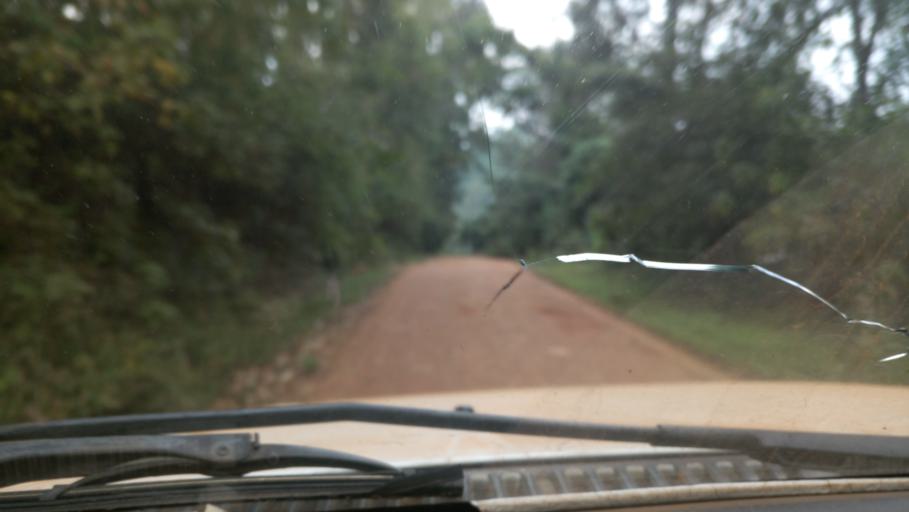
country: KE
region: Murang'a District
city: Kangema
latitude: -0.7140
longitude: 36.9963
